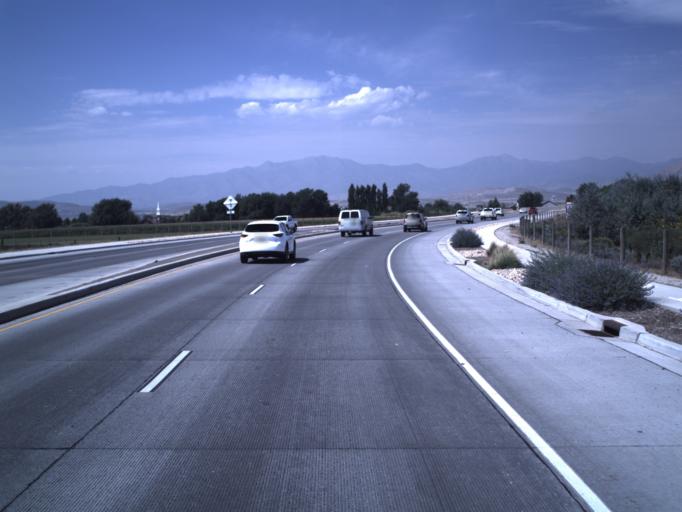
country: US
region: Utah
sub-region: Utah County
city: Lehi
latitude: 40.3753
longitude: -111.8681
